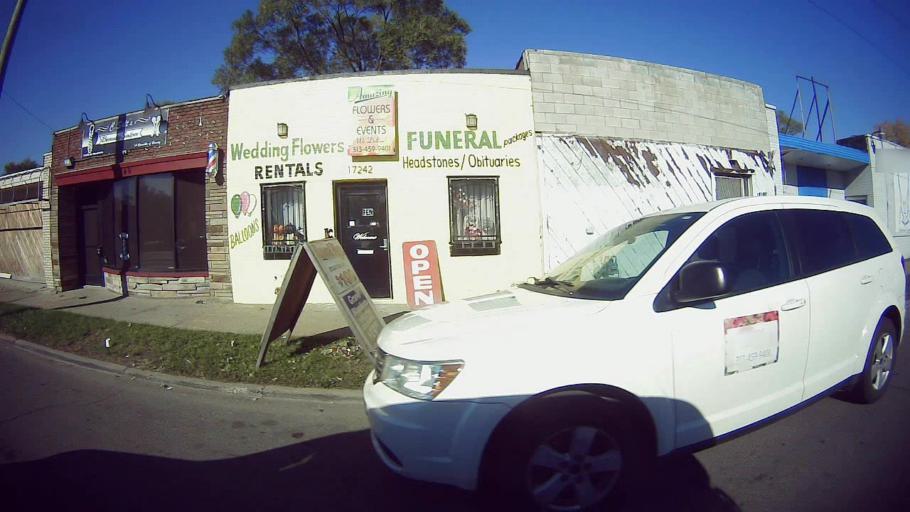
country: US
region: Michigan
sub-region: Oakland County
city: Oak Park
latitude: 42.4157
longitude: -83.2130
